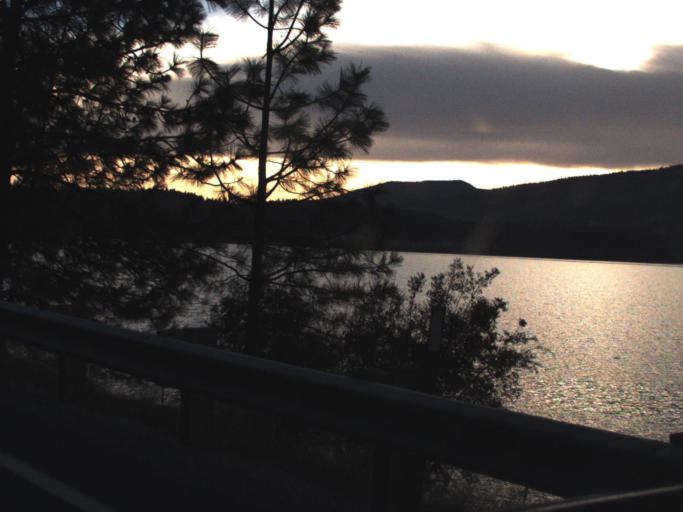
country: US
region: Washington
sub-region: Stevens County
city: Kettle Falls
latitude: 48.6391
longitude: -118.0826
